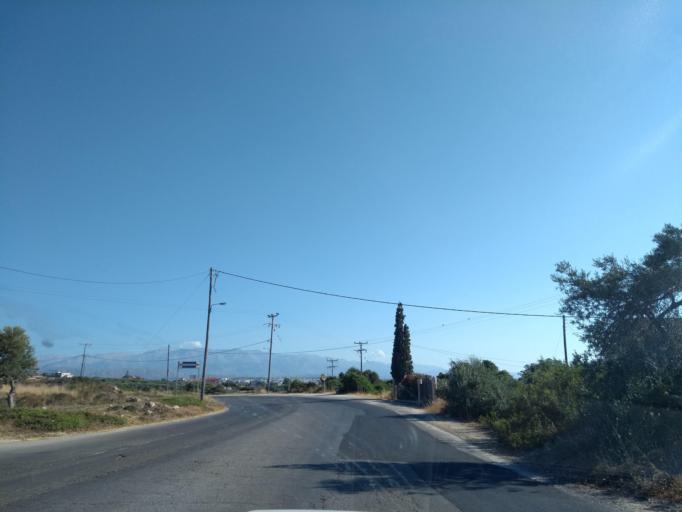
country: GR
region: Crete
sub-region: Nomos Chanias
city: Pithari
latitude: 35.5706
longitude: 24.0913
